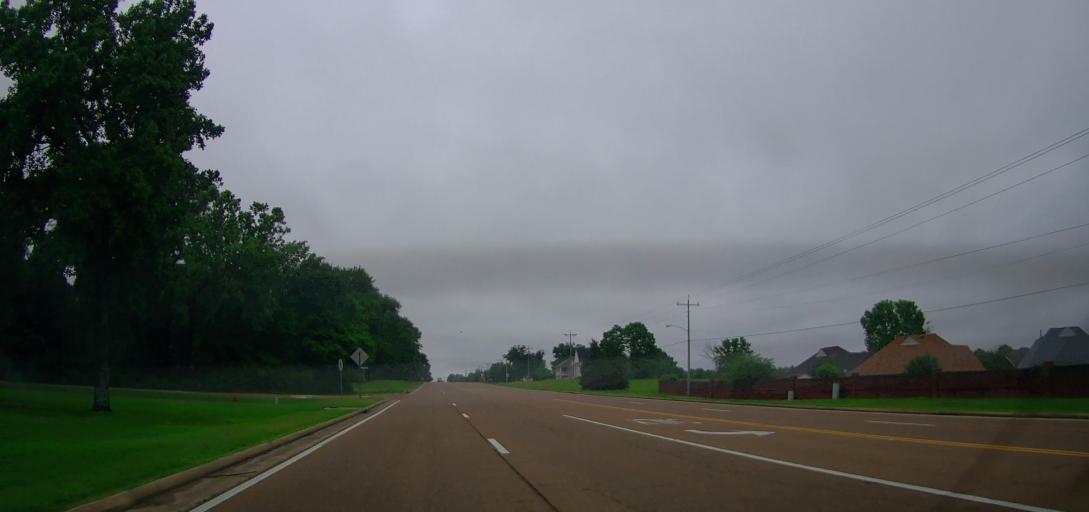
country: US
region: Mississippi
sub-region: De Soto County
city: Olive Branch
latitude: 34.9874
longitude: -89.8307
